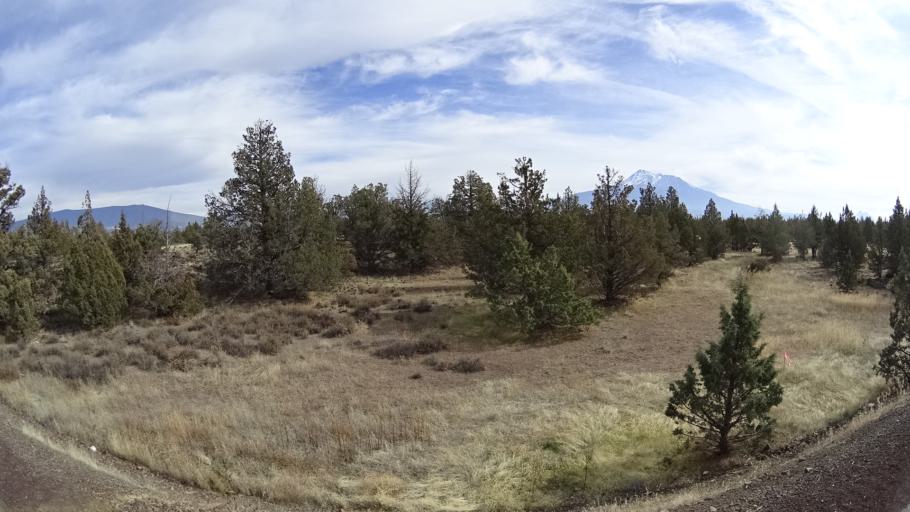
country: US
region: California
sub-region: Siskiyou County
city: Weed
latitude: 41.5911
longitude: -122.3999
